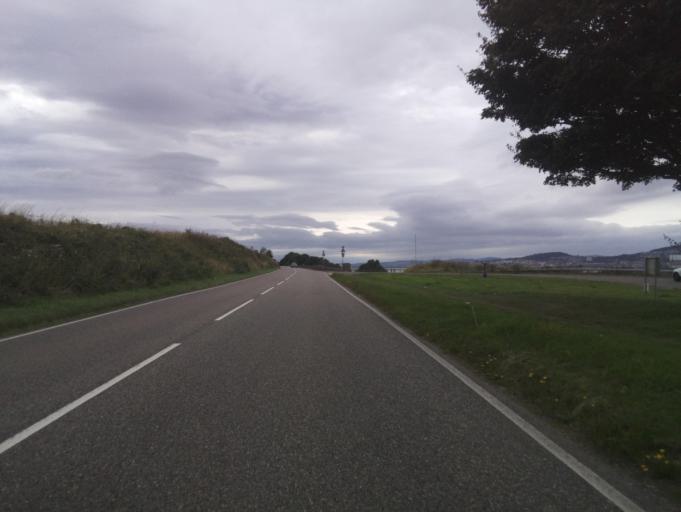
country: GB
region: Scotland
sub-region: Fife
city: Newport-On-Tay
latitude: 56.4499
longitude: -2.9177
